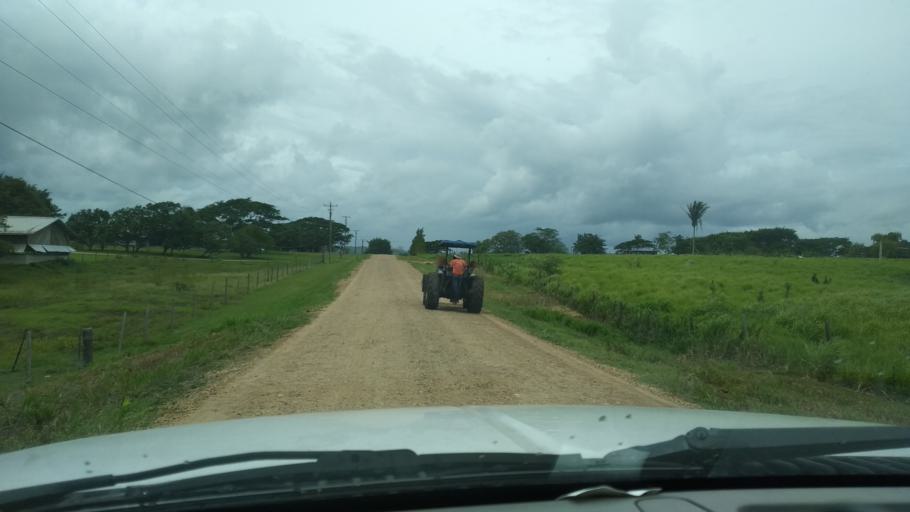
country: BZ
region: Cayo
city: San Ignacio
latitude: 17.2298
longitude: -88.9876
